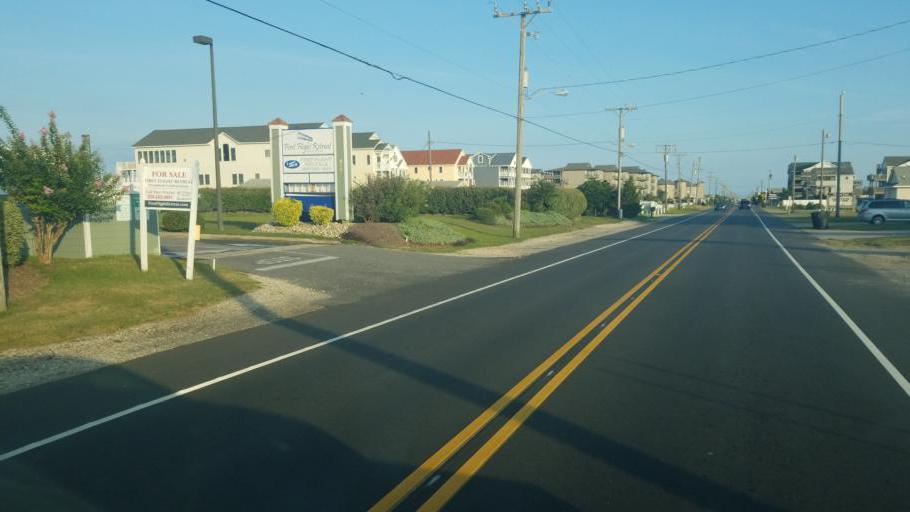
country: US
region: North Carolina
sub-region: Dare County
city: Kill Devil Hills
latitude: 36.0099
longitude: -75.6549
